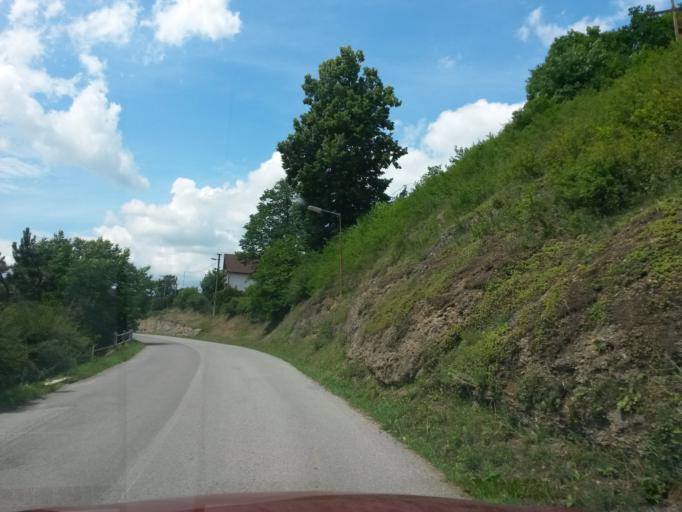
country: SK
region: Presovsky
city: Sabinov
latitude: 48.9665
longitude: 21.0892
